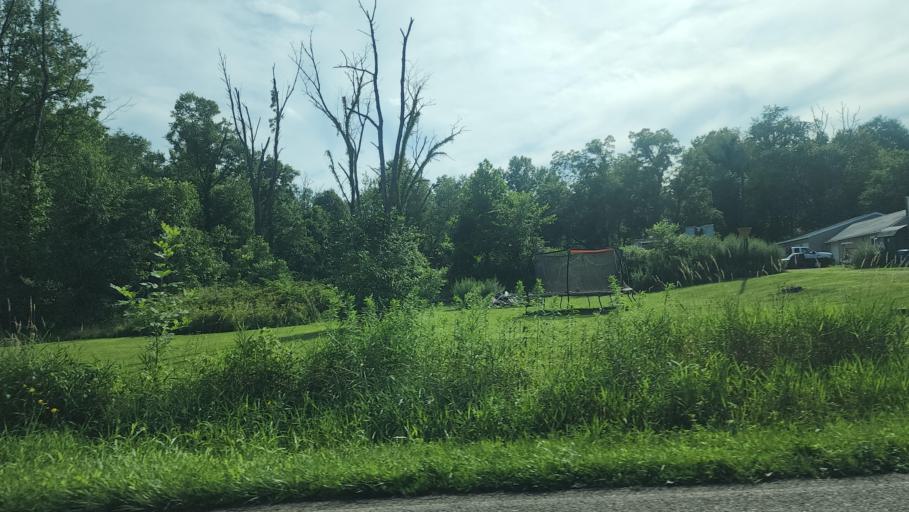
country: US
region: Ohio
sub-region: Trumbull County
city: Mineral Ridge
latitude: 41.1621
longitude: -80.7770
